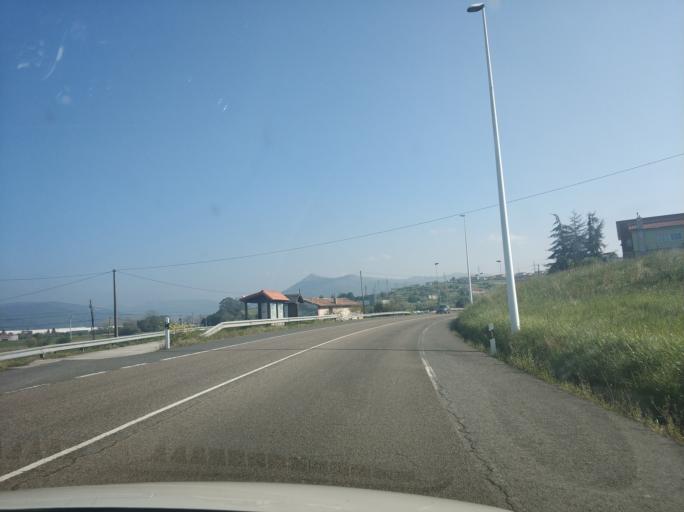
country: ES
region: Cantabria
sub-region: Provincia de Cantabria
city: Colindres
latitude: 43.4043
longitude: -3.4799
